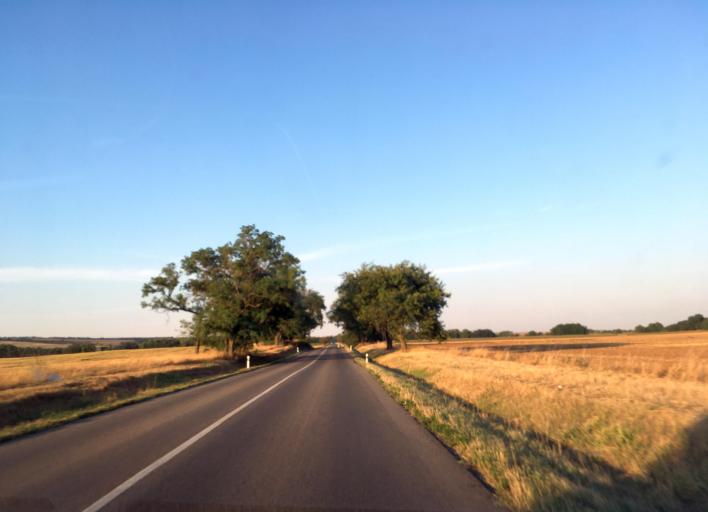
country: HU
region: Komarom-Esztergom
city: Dunaalmas
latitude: 47.7938
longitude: 18.2990
